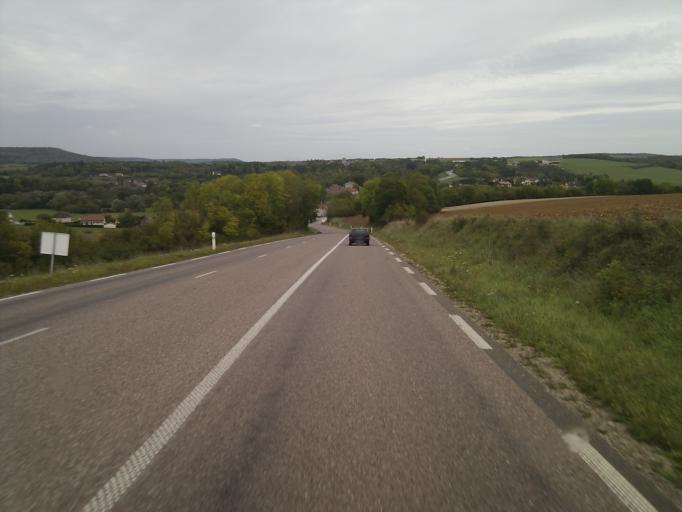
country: FR
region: Lorraine
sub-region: Departement des Vosges
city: Neufchateau
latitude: 48.3970
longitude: 5.7271
